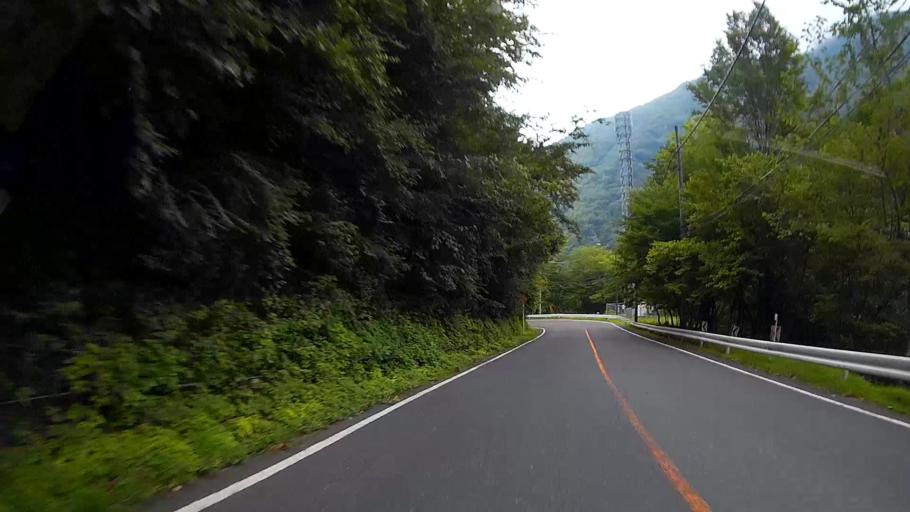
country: JP
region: Yamanashi
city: Enzan
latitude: 35.9137
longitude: 138.8252
